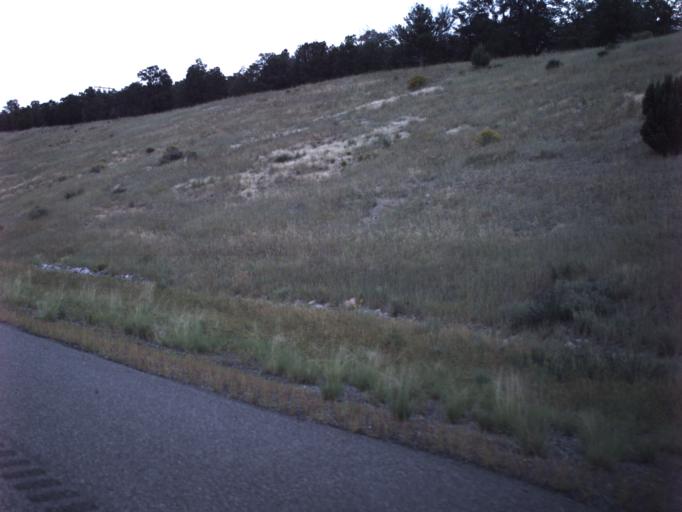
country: US
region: Utah
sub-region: Sevier County
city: Monroe
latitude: 38.5509
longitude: -112.3676
